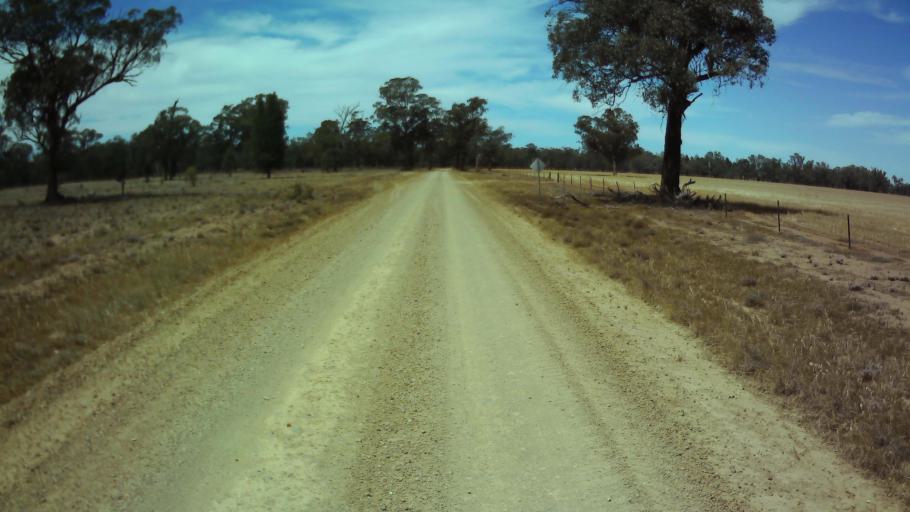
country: AU
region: New South Wales
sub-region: Weddin
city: Grenfell
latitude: -33.8515
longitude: 147.8060
